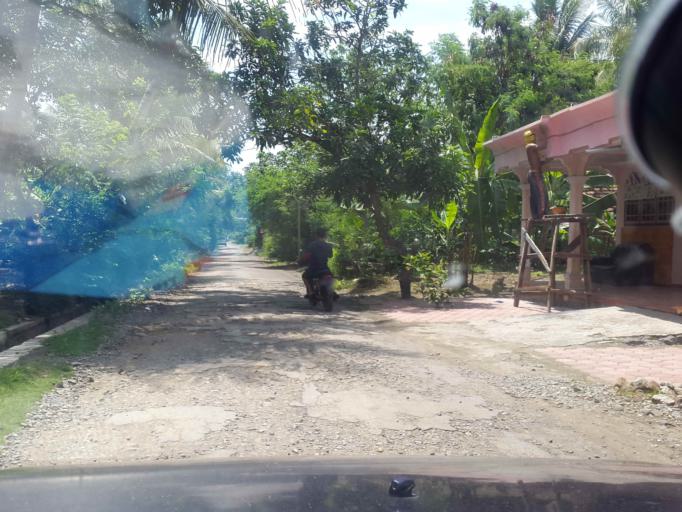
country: ID
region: East Java
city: Ketawang
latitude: -8.2786
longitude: 111.7243
